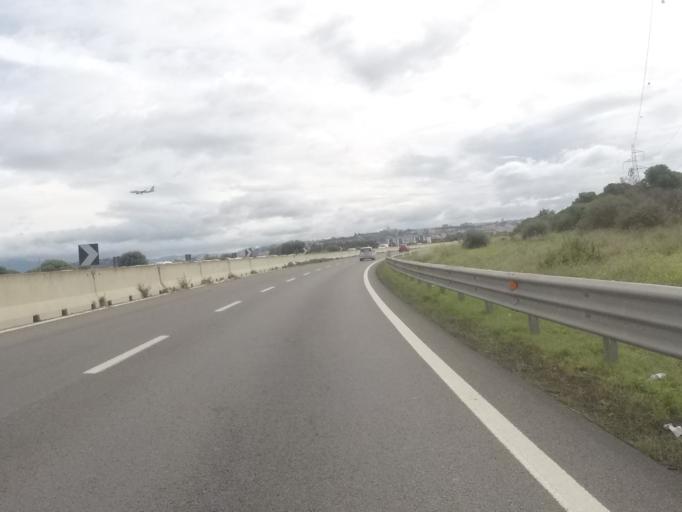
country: IT
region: Sardinia
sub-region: Provincia di Cagliari
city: Su Planu
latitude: 39.2263
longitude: 9.0703
